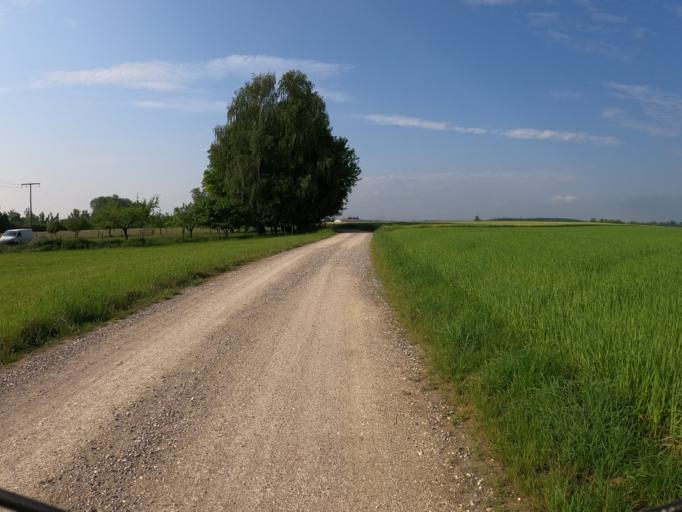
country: DE
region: Bavaria
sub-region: Swabia
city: Pfaffenhofen an der Roth
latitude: 48.3746
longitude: 10.1483
